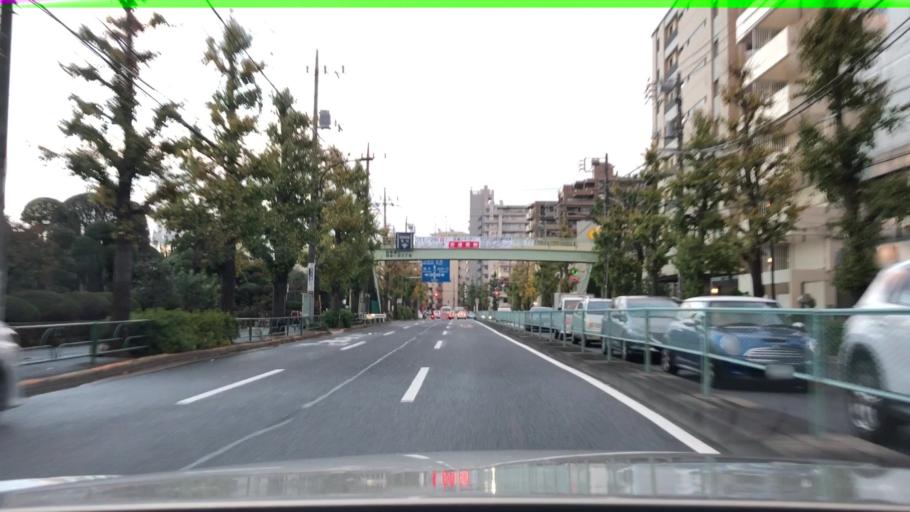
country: JP
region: Tokyo
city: Tokyo
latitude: 35.6138
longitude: 139.6644
